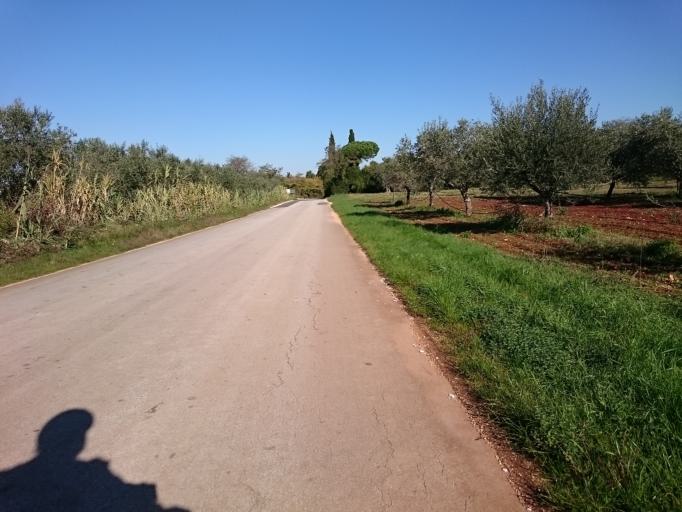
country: HR
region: Istarska
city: Umag
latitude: 45.3862
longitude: 13.5380
